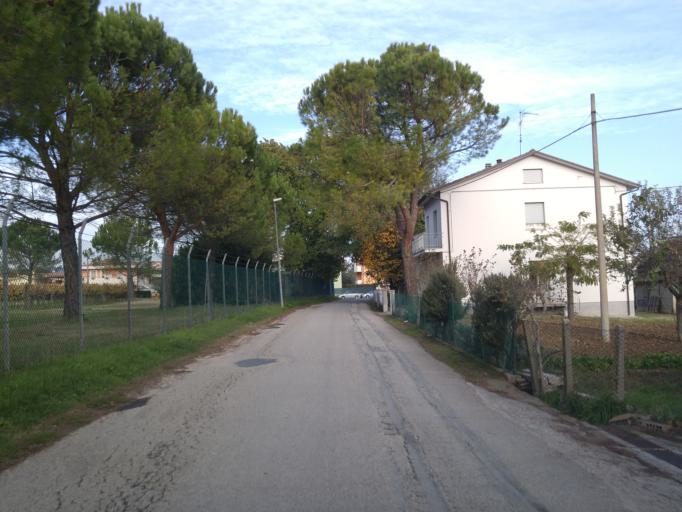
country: IT
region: The Marches
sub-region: Provincia di Pesaro e Urbino
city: Lucrezia
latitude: 43.7803
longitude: 12.9393
